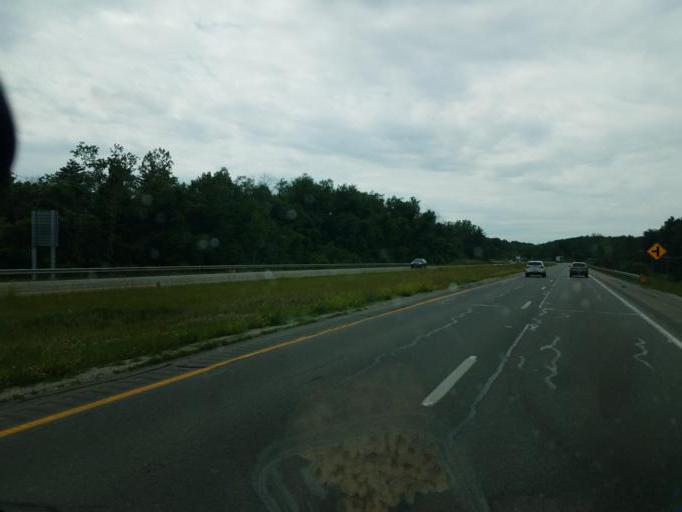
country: US
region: Ohio
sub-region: Richland County
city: Lincoln Heights
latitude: 40.7841
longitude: -82.3871
